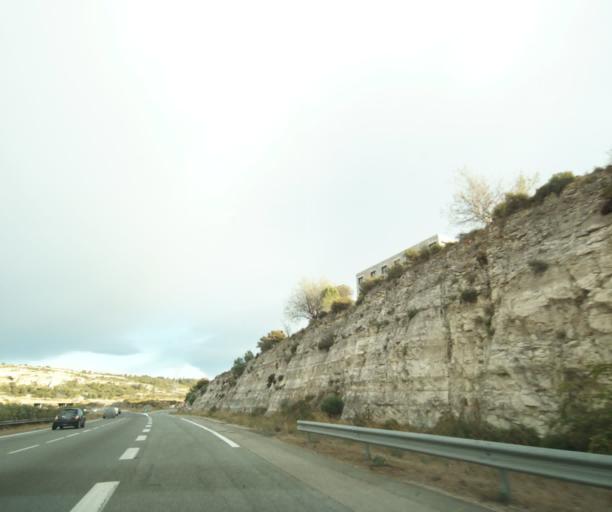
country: FR
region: Provence-Alpes-Cote d'Azur
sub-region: Departement des Bouches-du-Rhone
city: Gignac-la-Nerthe
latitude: 43.3800
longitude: 5.2182
